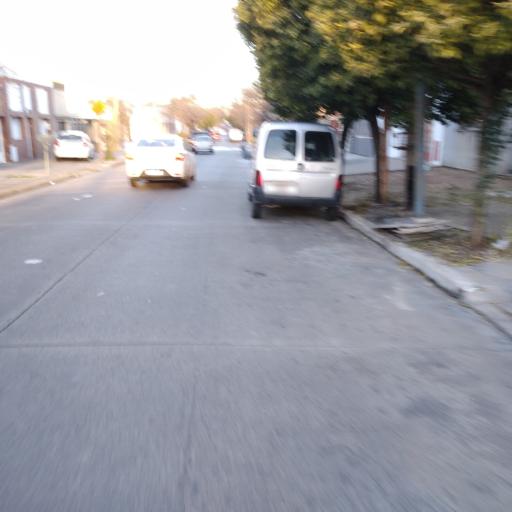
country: AR
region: Buenos Aires
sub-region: Partido de La Plata
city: La Plata
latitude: -34.9388
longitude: -57.9679
